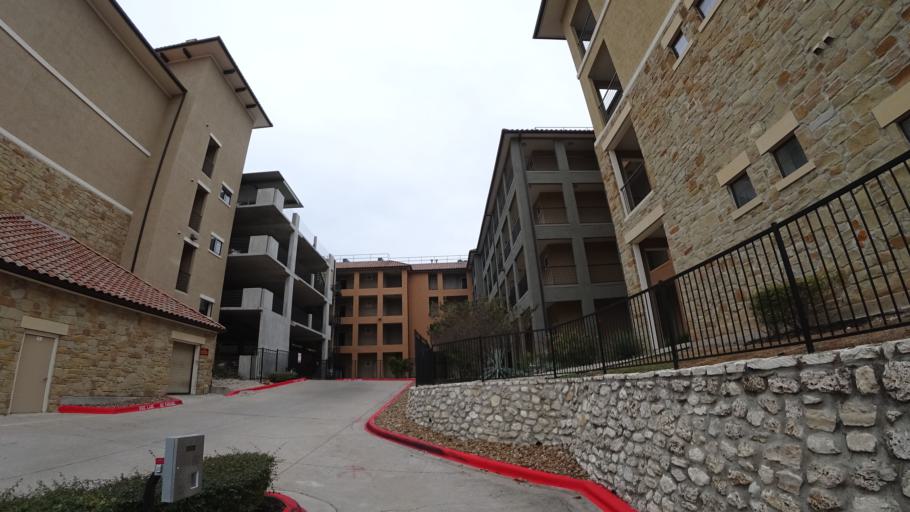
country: US
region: Texas
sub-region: Travis County
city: West Lake Hills
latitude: 30.3700
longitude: -97.8072
